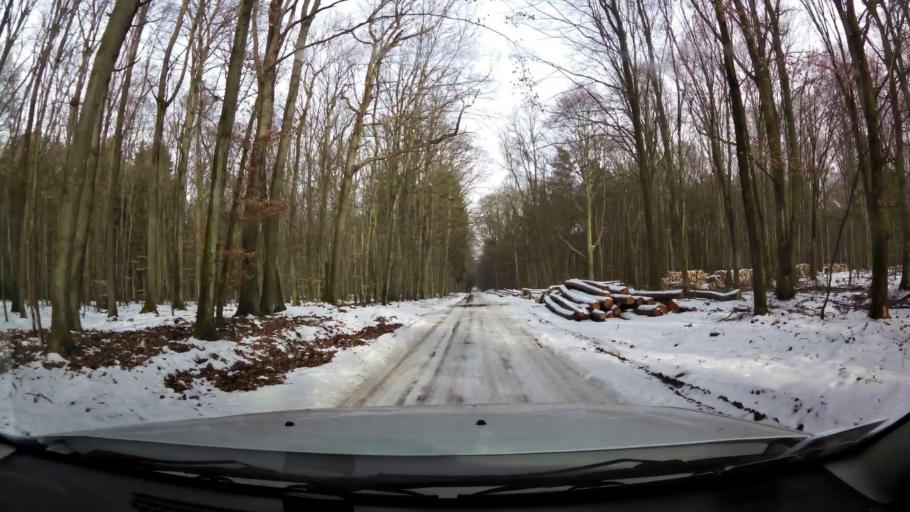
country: PL
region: West Pomeranian Voivodeship
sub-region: Powiat kamienski
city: Miedzyzdroje
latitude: 53.8869
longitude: 14.4919
